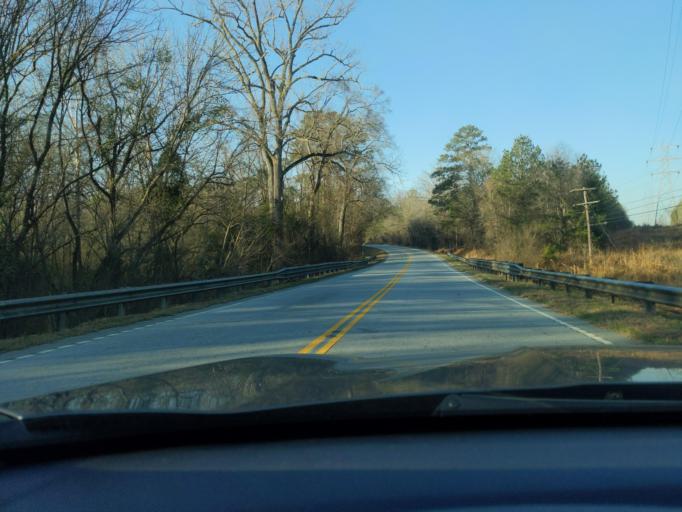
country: US
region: South Carolina
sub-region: Newberry County
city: Newberry
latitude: 34.2569
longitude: -81.6344
